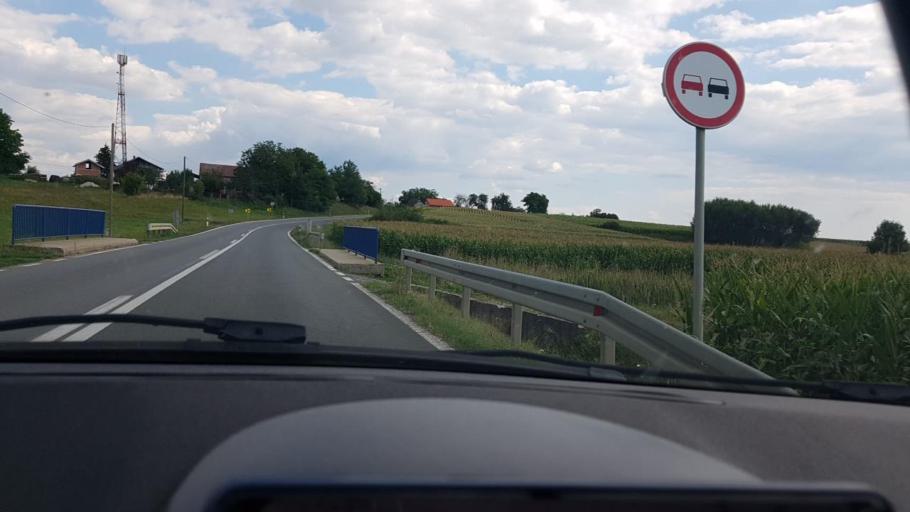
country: HR
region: Bjelovarsko-Bilogorska
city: Zdralovi
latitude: 45.8609
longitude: 16.9219
